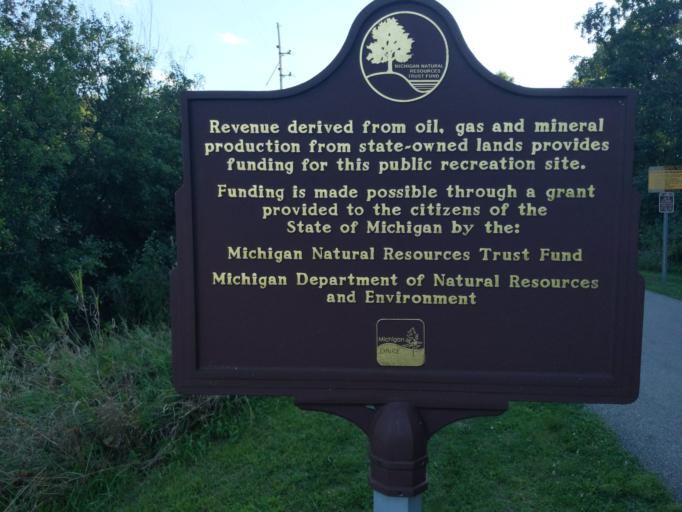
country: US
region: Michigan
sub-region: Jackson County
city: Vandercook Lake
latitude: 42.2100
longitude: -84.4418
